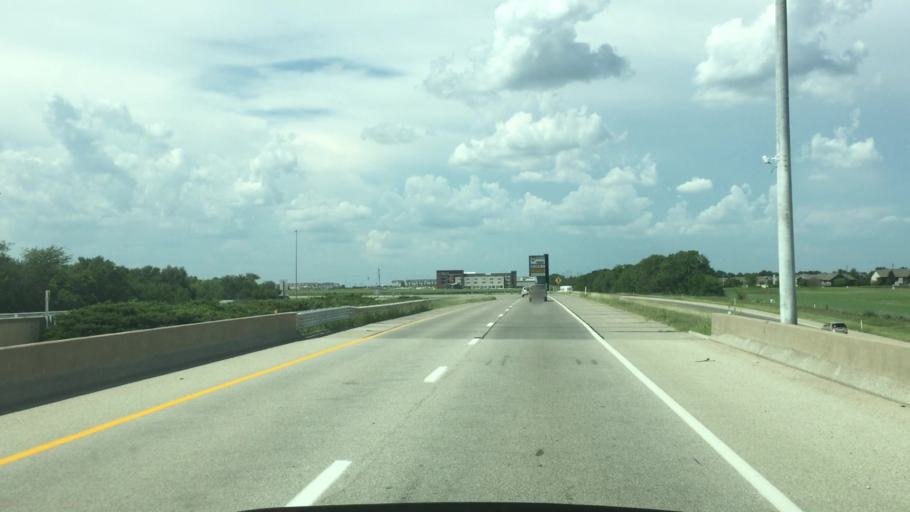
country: US
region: Kansas
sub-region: Butler County
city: Andover
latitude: 37.7232
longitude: -97.1993
